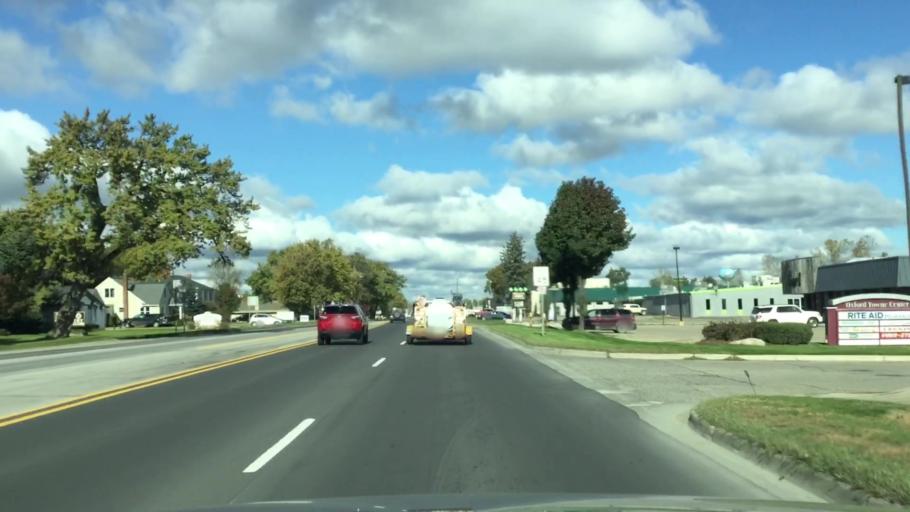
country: US
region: Michigan
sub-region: Oakland County
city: Oxford
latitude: 42.8112
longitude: -83.2524
